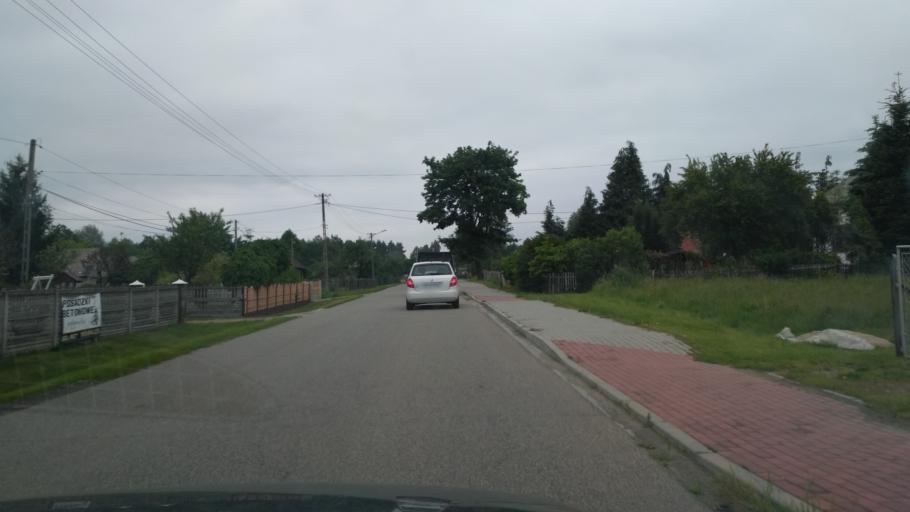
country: PL
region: Subcarpathian Voivodeship
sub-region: Powiat ropczycko-sedziszowski
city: Sedziszow Malopolski
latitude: 50.1471
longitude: 21.6703
